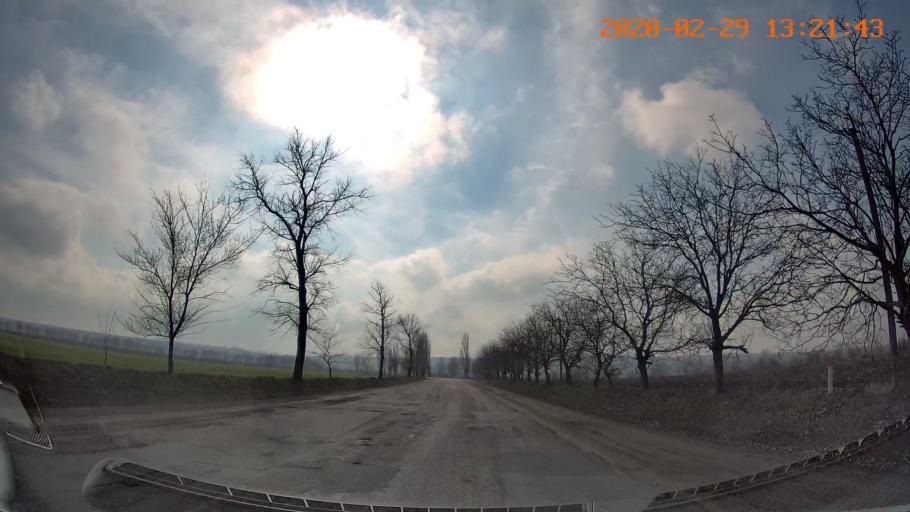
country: MD
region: Telenesti
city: Camenca
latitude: 47.9678
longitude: 28.6306
